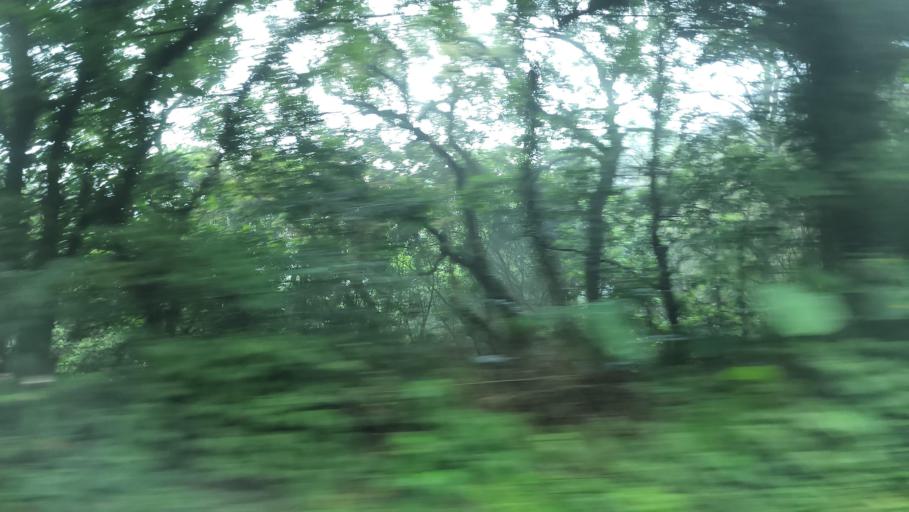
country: TW
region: Taipei
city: Taipei
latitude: 25.1425
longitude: 121.6023
